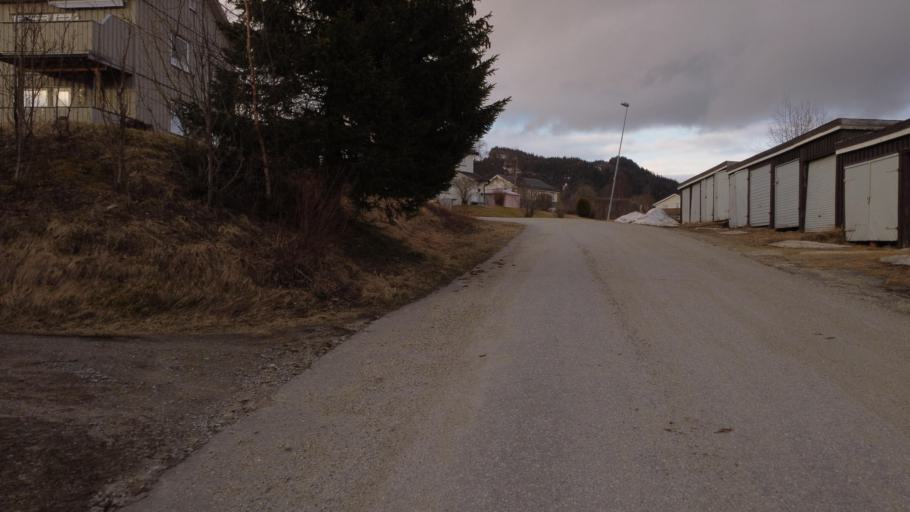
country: NO
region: Nordland
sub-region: Rana
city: Mo i Rana
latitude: 66.3254
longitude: 14.1709
